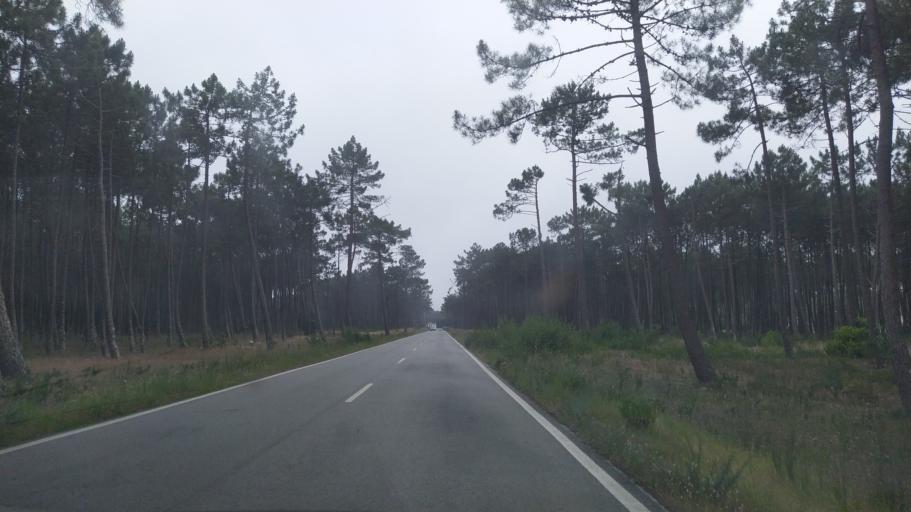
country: PT
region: Aveiro
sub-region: Ilhavo
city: Gafanha da Encarnacao
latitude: 40.5841
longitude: -8.7311
